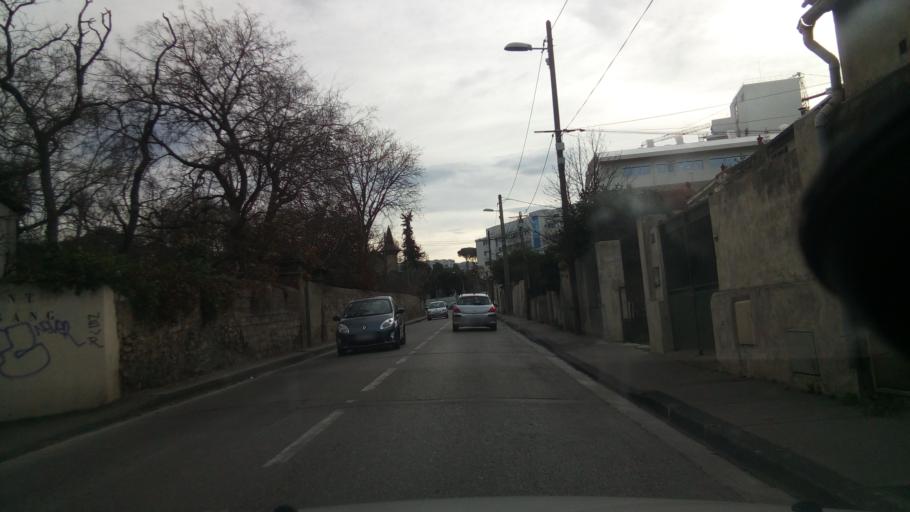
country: FR
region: Provence-Alpes-Cote d'Azur
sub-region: Departement des Bouches-du-Rhone
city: Marseille 09
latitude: 43.2645
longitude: 5.4098
